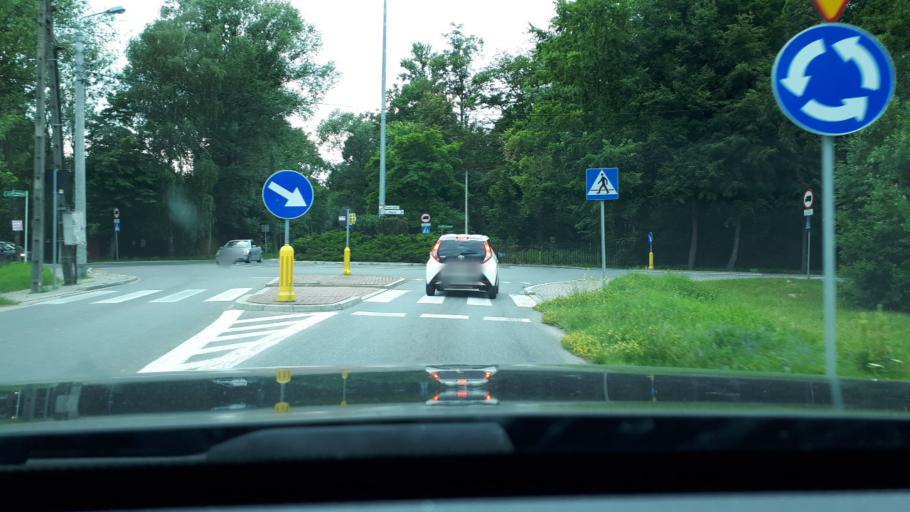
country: PL
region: Masovian Voivodeship
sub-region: Powiat pruszkowski
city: Komorow
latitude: 52.1444
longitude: 20.8482
